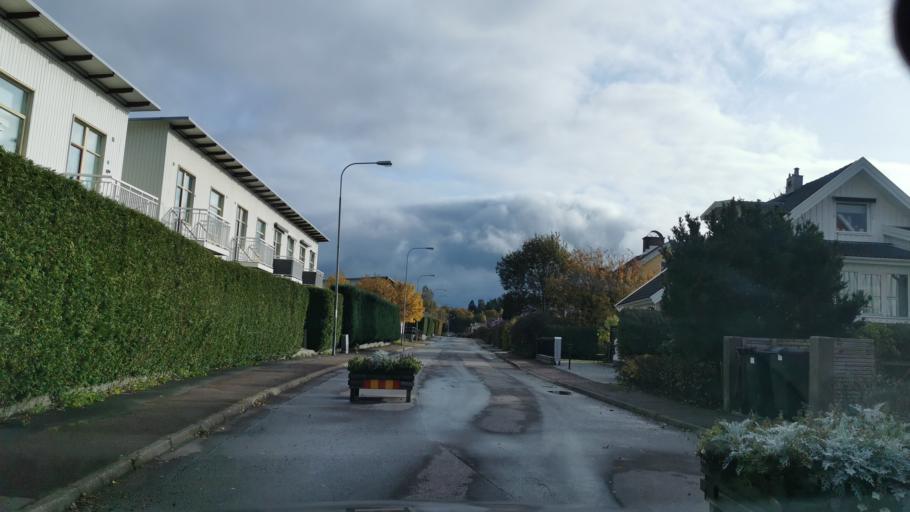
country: SE
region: Vaestra Goetaland
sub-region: Partille Kommun
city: Partille
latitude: 57.7272
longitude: 12.0818
